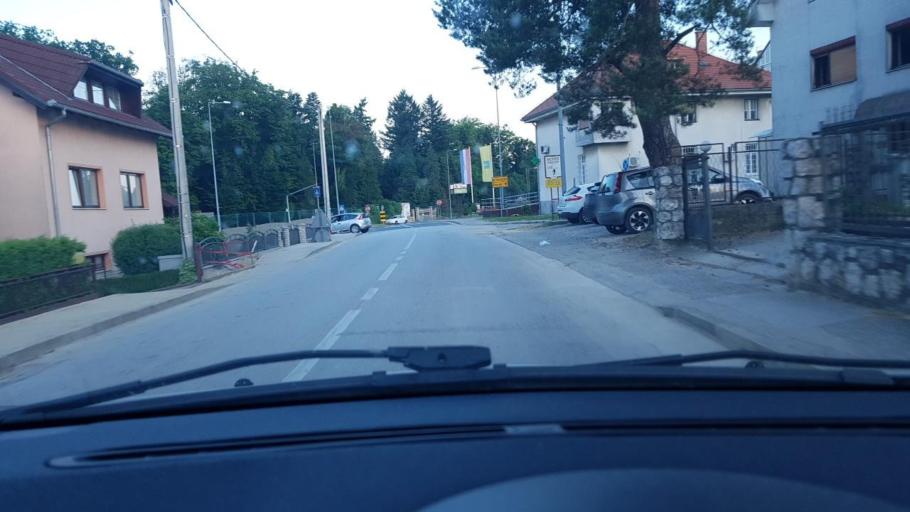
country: HR
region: Varazdinska
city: Remetinec
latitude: 46.1674
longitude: 16.3343
